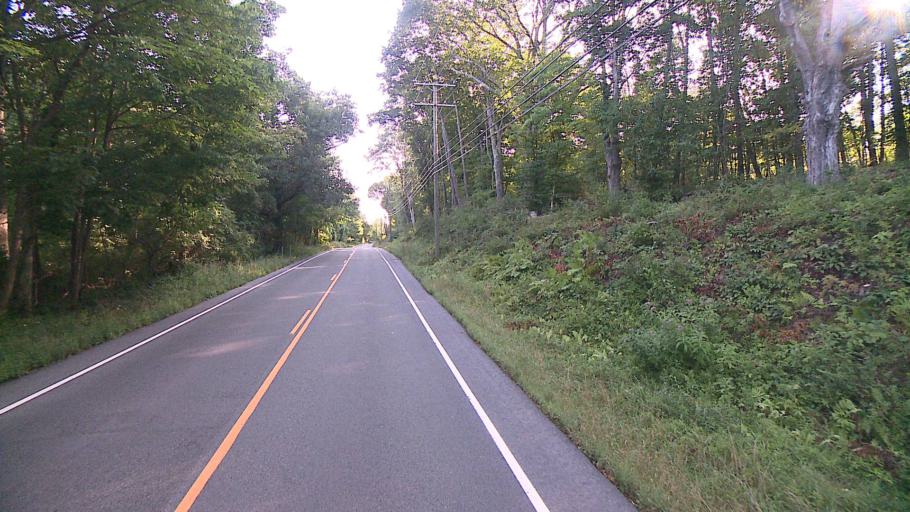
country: US
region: Connecticut
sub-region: Litchfield County
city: Kent
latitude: 41.7607
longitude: -73.4354
